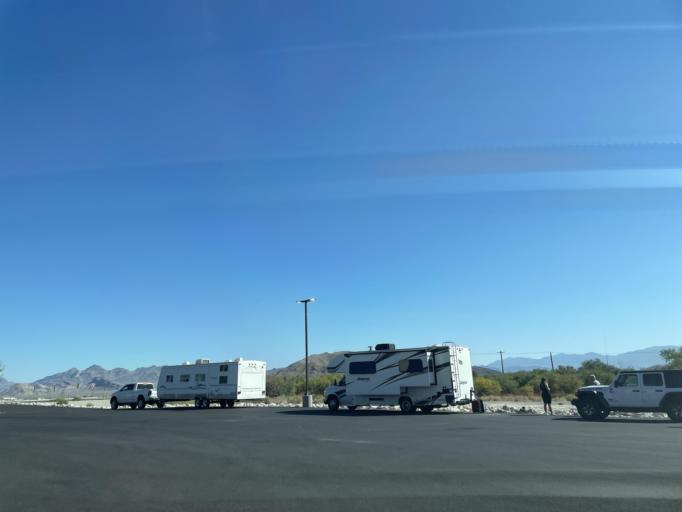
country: US
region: Nevada
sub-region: Nye County
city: Pahrump
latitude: 36.5769
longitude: -115.6682
